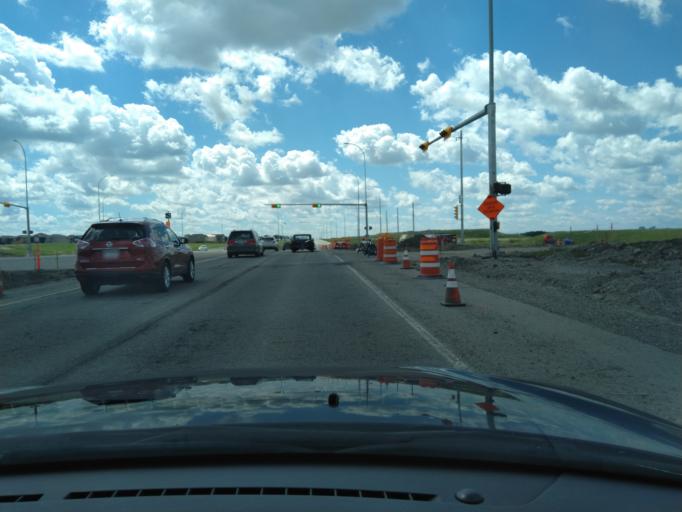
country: CA
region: Alberta
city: Calgary
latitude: 51.1402
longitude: -113.9703
